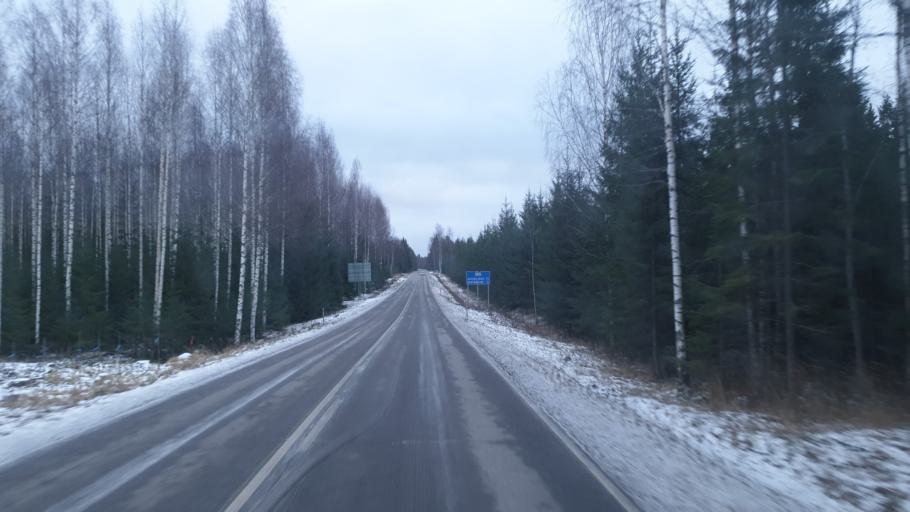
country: FI
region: Southern Savonia
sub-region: Pieksaemaeki
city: Joroinen
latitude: 62.2233
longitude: 27.8939
